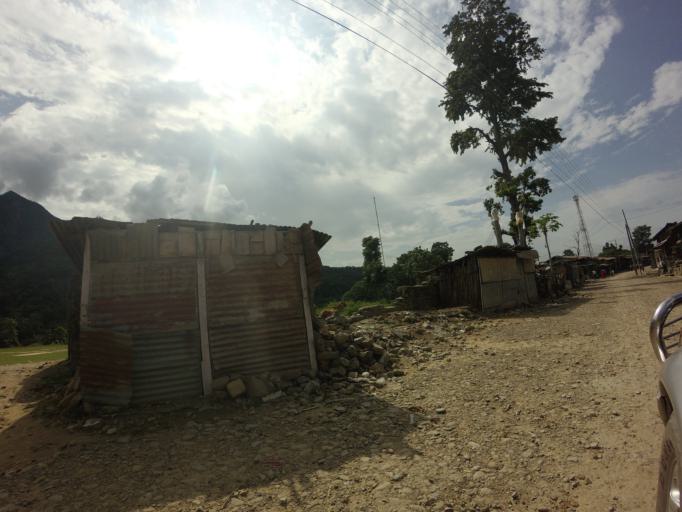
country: NP
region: Far Western
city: Tikapur
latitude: 28.6463
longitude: 81.2843
